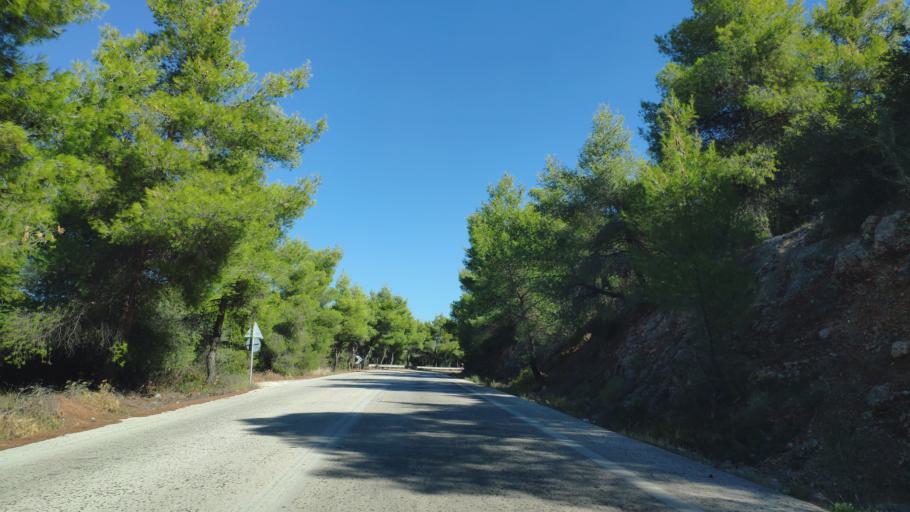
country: GR
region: Peloponnese
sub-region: Nomos Korinthias
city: Sofikon
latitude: 37.8285
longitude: 23.0460
